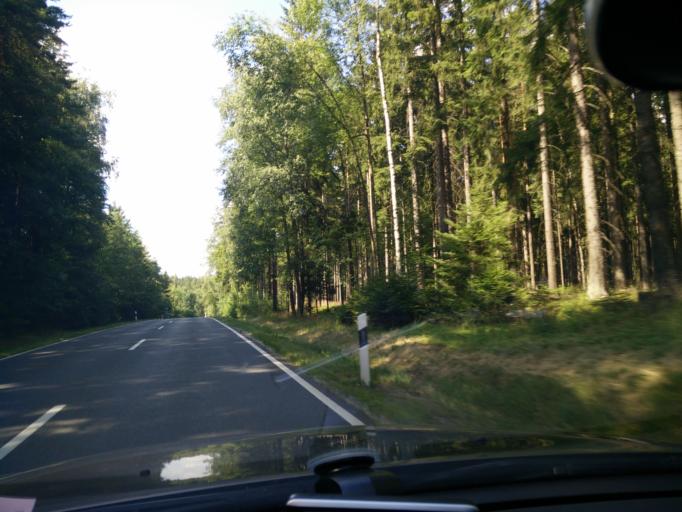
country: DE
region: Bavaria
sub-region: Upper Franconia
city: Roslau
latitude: 50.0572
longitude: 11.9742
